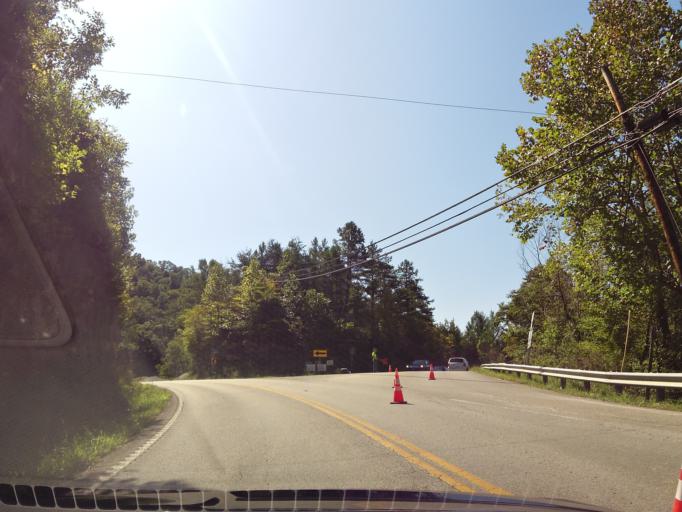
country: US
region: Kentucky
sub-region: Clay County
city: Manchester
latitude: 37.0865
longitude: -83.6909
